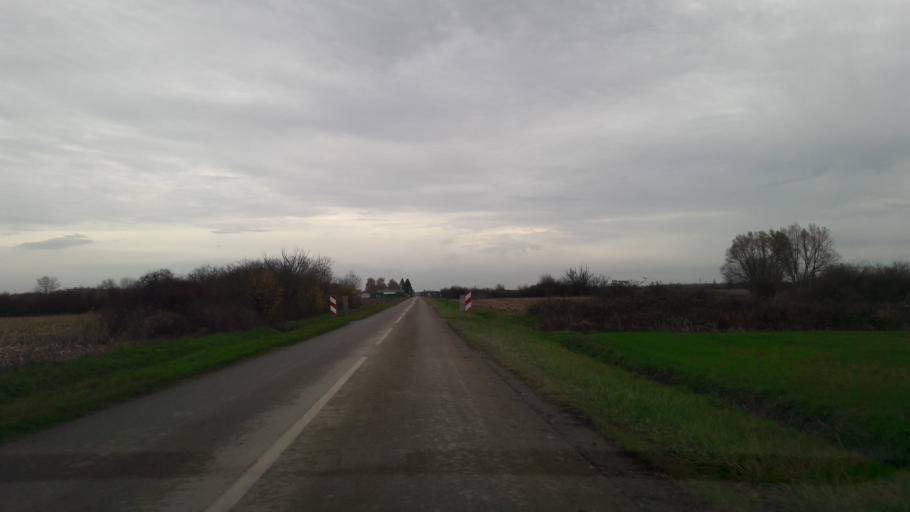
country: HR
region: Osjecko-Baranjska
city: Jelisavac
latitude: 45.6381
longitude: 18.1286
